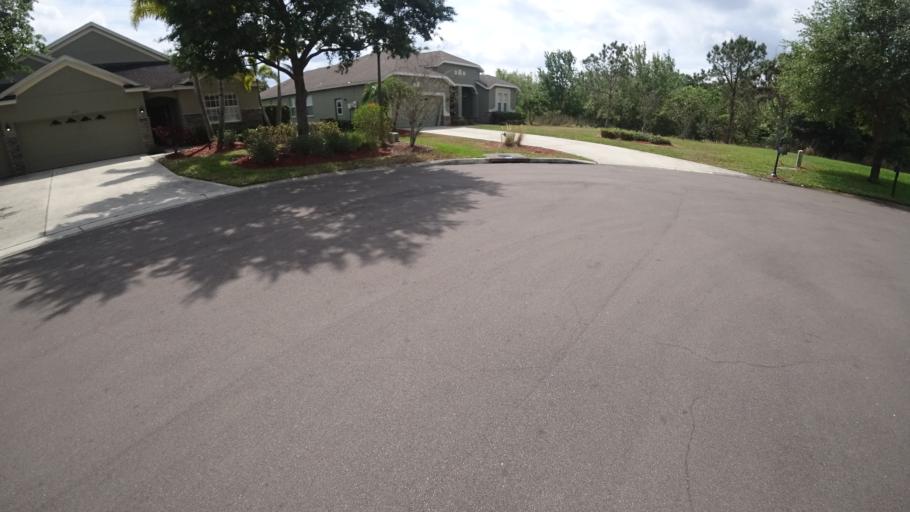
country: US
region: Florida
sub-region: Manatee County
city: Ellenton
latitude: 27.5315
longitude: -82.4219
